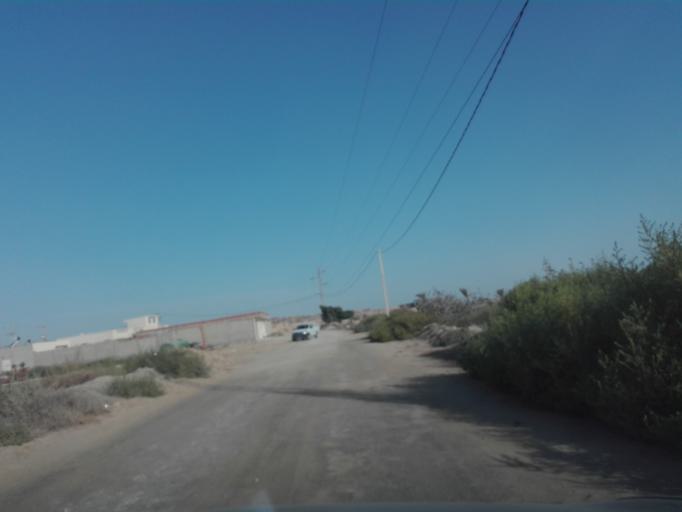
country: TN
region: Qabis
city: Gabes
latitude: 33.9597
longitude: 10.0614
